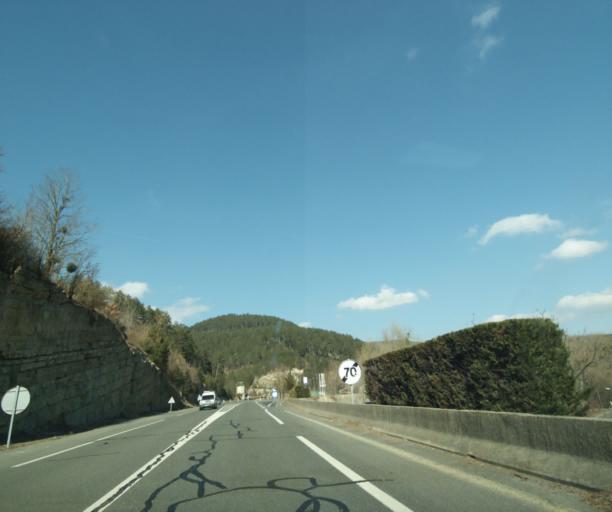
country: FR
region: Languedoc-Roussillon
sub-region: Departement de la Lozere
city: Mende
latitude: 44.5252
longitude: 3.5215
